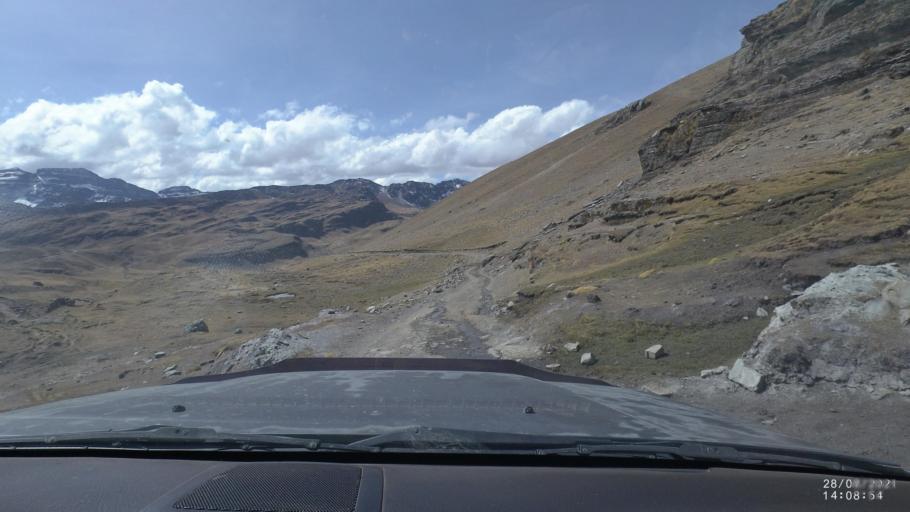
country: BO
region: Cochabamba
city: Sipe Sipe
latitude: -17.2635
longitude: -66.3839
